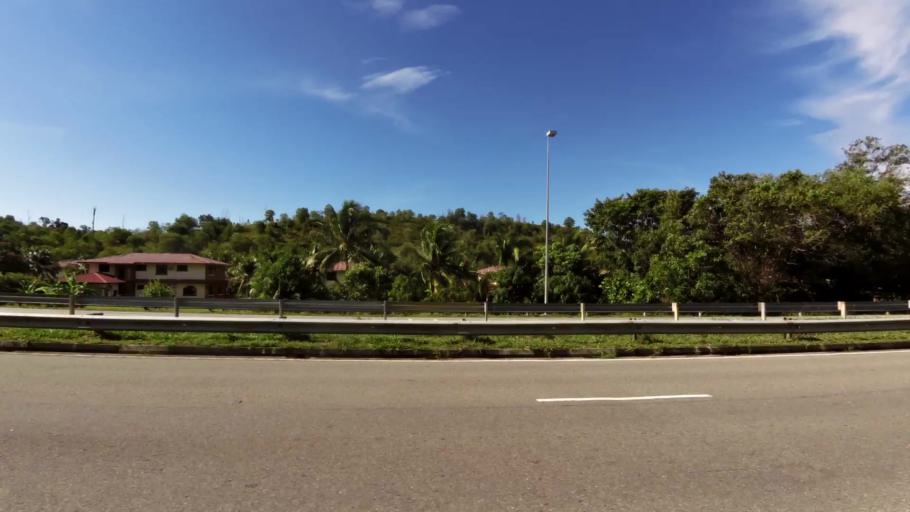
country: BN
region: Brunei and Muara
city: Bandar Seri Begawan
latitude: 4.9821
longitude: 114.9332
